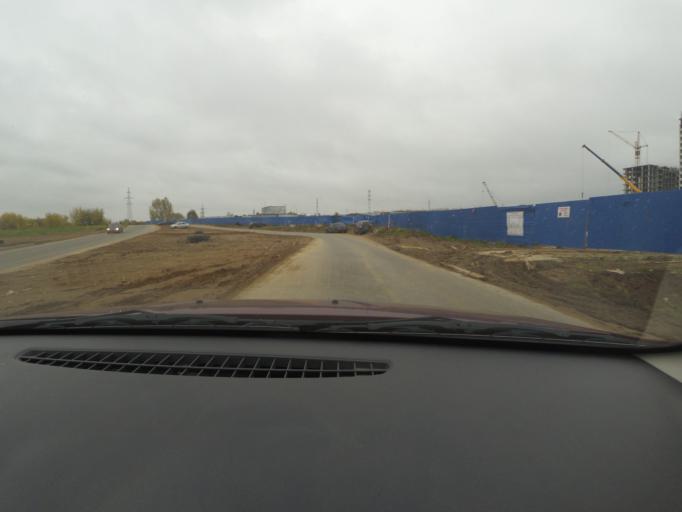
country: RU
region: Nizjnij Novgorod
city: Afonino
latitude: 56.2767
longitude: 44.0526
